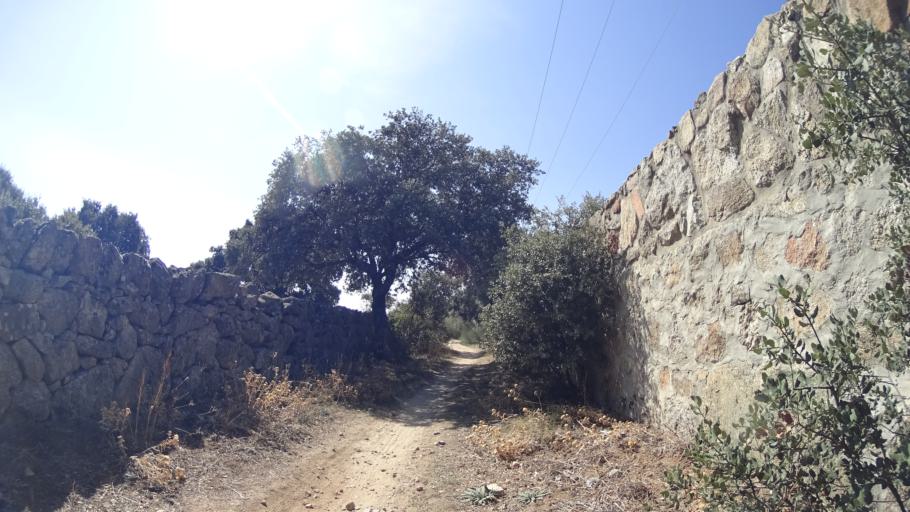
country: ES
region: Madrid
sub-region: Provincia de Madrid
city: Colmenarejo
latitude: 40.5697
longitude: -4.0263
